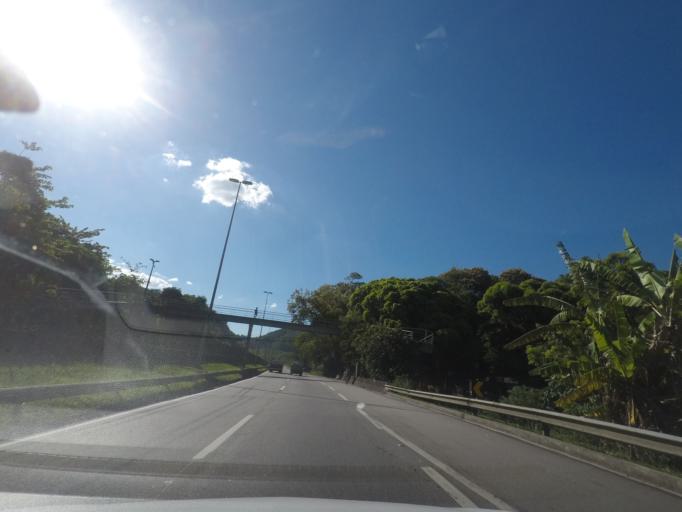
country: BR
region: Rio de Janeiro
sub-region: Petropolis
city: Petropolis
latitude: -22.6581
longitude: -43.1177
